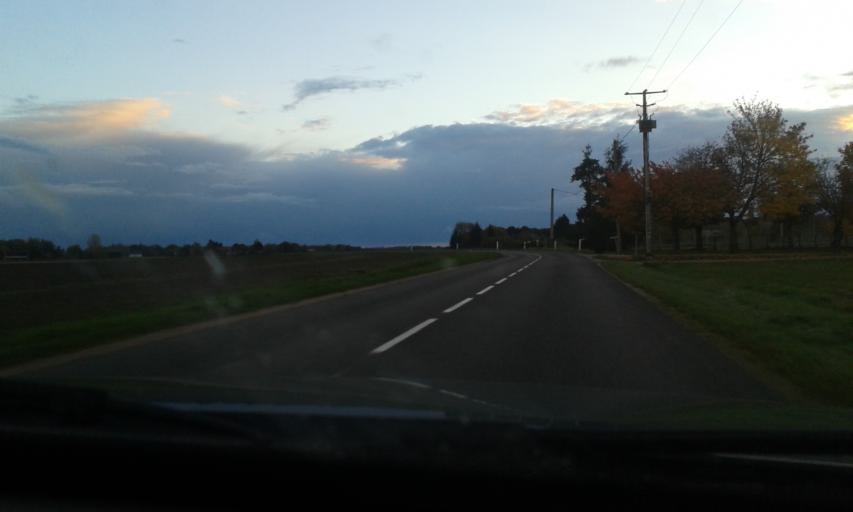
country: FR
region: Centre
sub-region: Departement du Loiret
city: Huisseau-sur-Mauves
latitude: 47.9205
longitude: 1.6988
